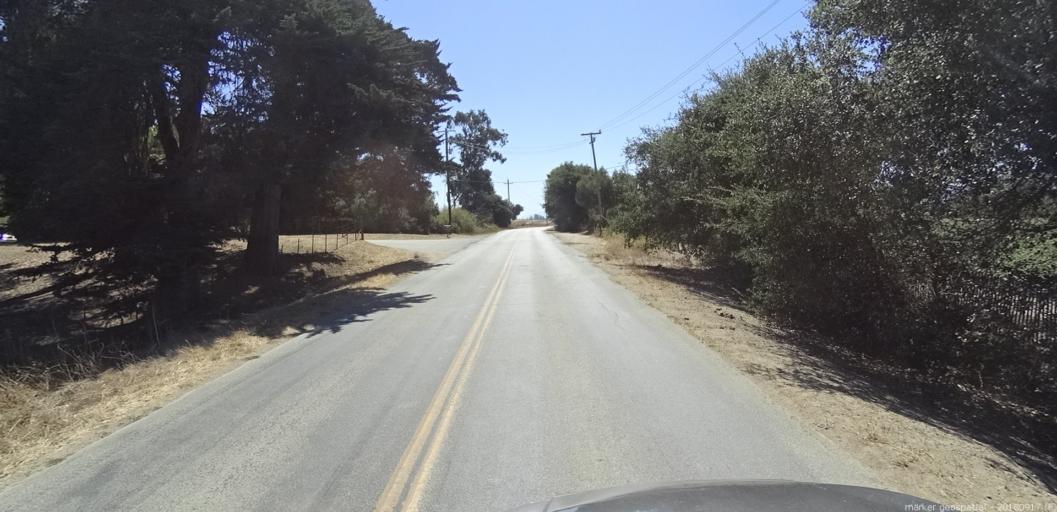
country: US
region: California
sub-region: Monterey County
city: Salinas
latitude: 36.7305
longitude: -121.5961
